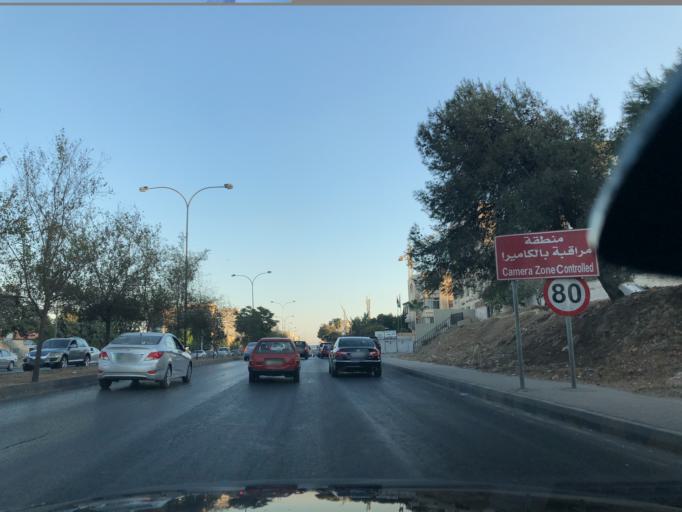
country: JO
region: Amman
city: Wadi as Sir
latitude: 31.9696
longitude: 35.8409
